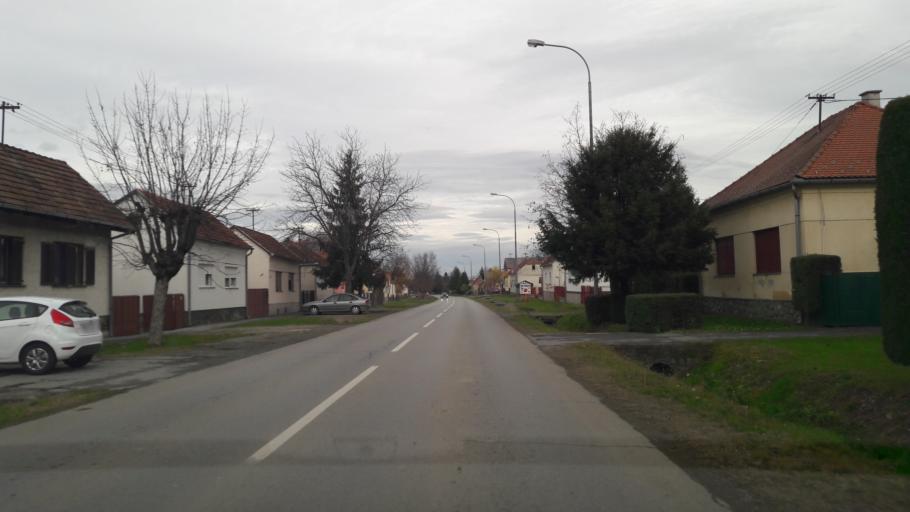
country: HR
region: Virovitick-Podravska
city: Orahovica
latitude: 45.5416
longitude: 17.8971
